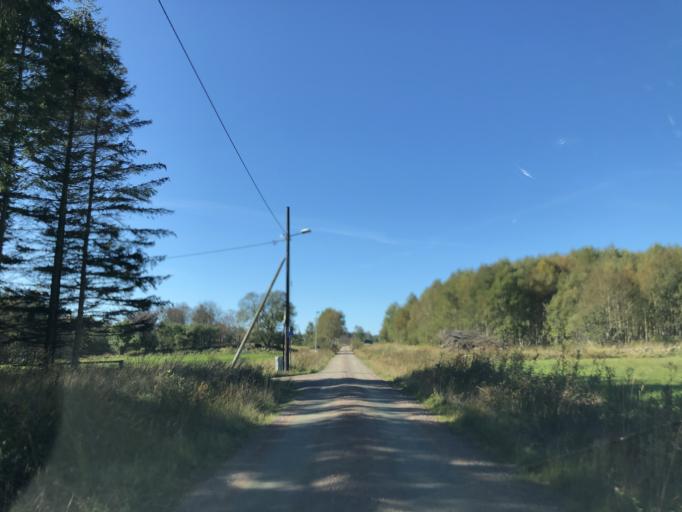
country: SE
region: Vaestra Goetaland
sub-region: Goteborg
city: Majorna
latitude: 57.7647
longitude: 11.9125
